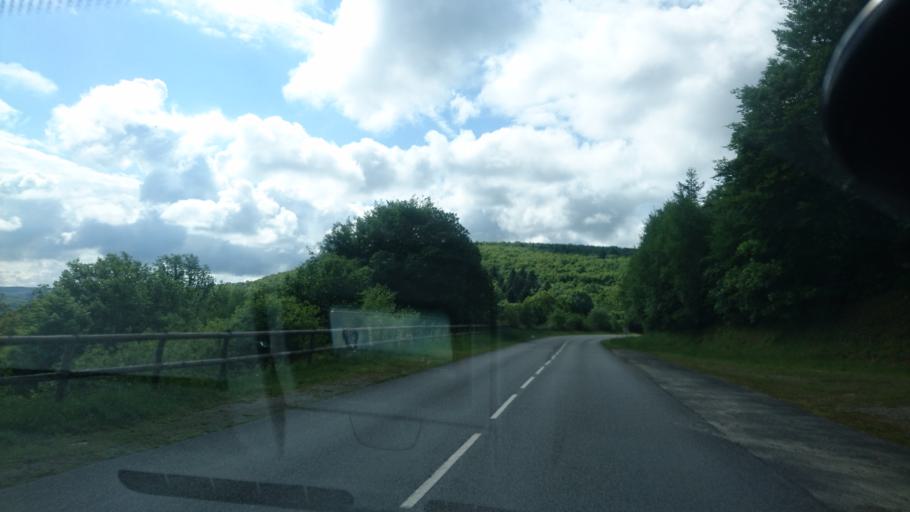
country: FR
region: Limousin
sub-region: Departement de la Haute-Vienne
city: Peyrat-le-Chateau
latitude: 45.7985
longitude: 1.8409
